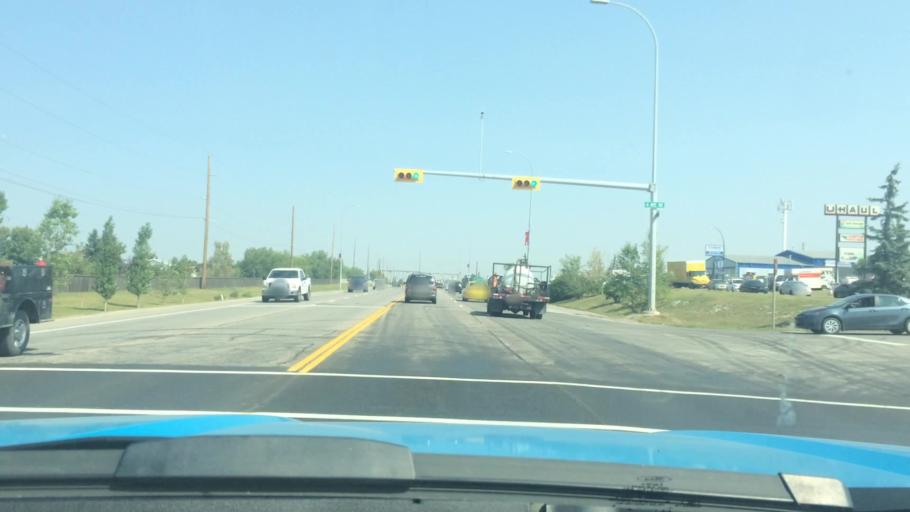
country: CA
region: Alberta
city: Calgary
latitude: 51.0553
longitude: -114.0017
